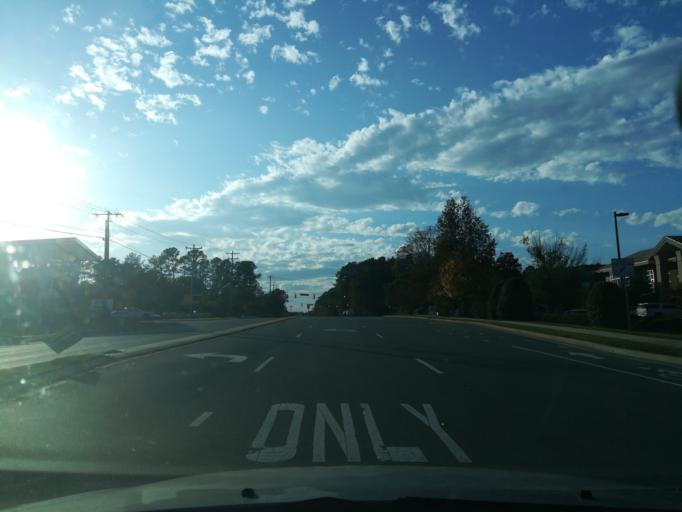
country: US
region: North Carolina
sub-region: Orange County
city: Chapel Hill
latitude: 35.9641
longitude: -79.0565
